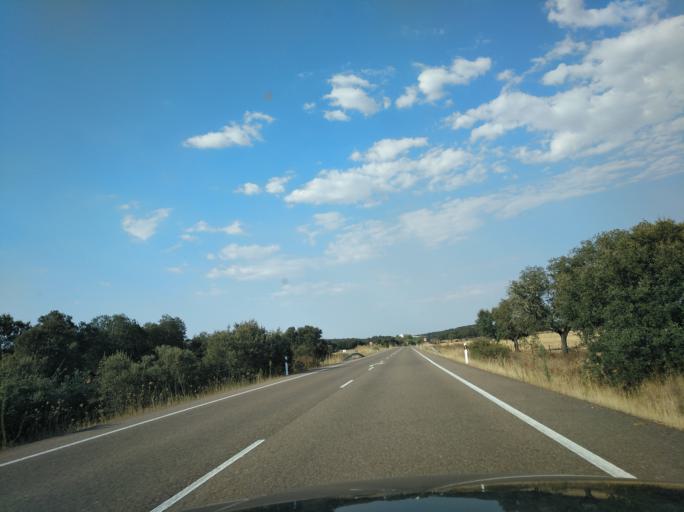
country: ES
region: Extremadura
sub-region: Provincia de Badajoz
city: Alconchel
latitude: 38.4683
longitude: -7.0730
